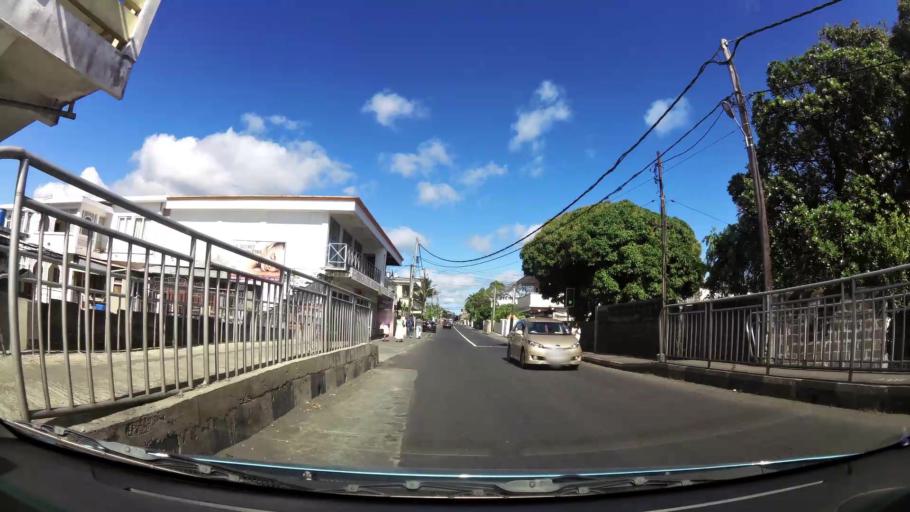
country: MU
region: Plaines Wilhems
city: Vacoas
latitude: -20.3059
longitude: 57.4919
